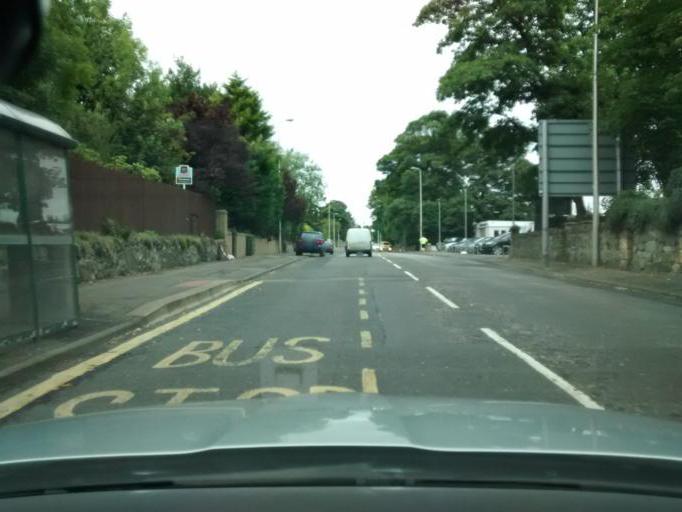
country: GB
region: Scotland
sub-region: West Lothian
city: Bathgate
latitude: 55.8952
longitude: -3.6227
